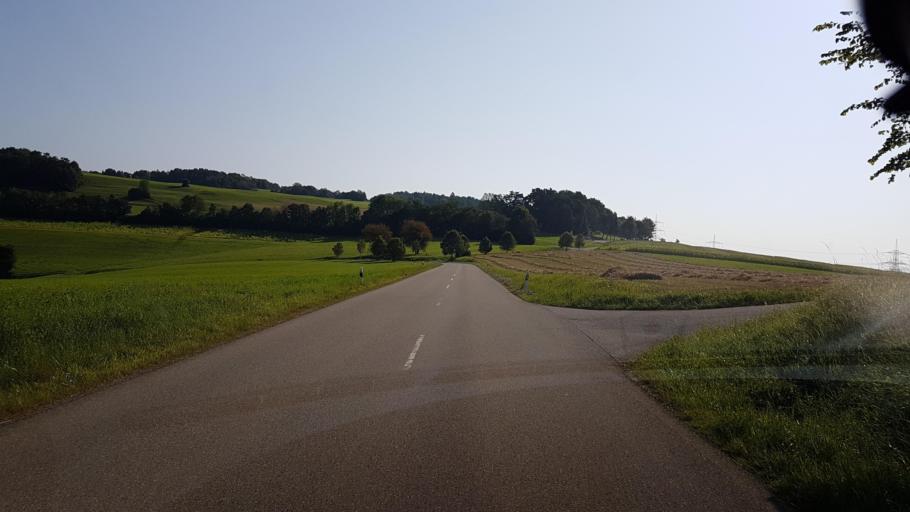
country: DE
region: Baden-Wuerttemberg
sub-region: Freiburg Region
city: Gorwihl
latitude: 47.6244
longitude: 8.1112
